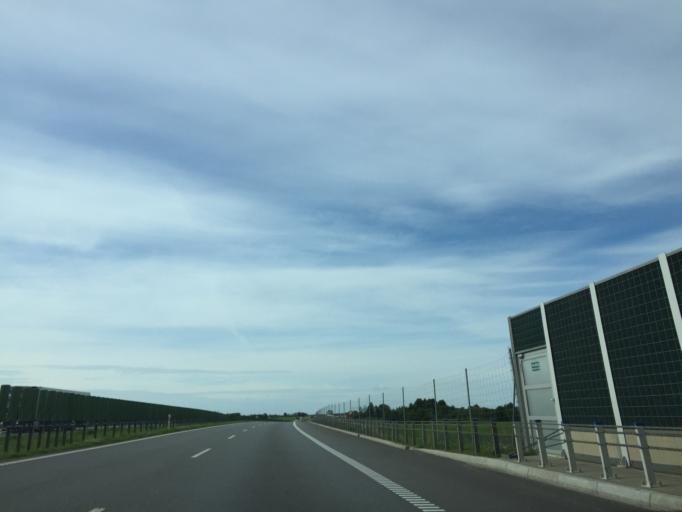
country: PL
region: Podlasie
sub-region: Suwalki
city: Suwalki
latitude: 54.0374
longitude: 22.8912
